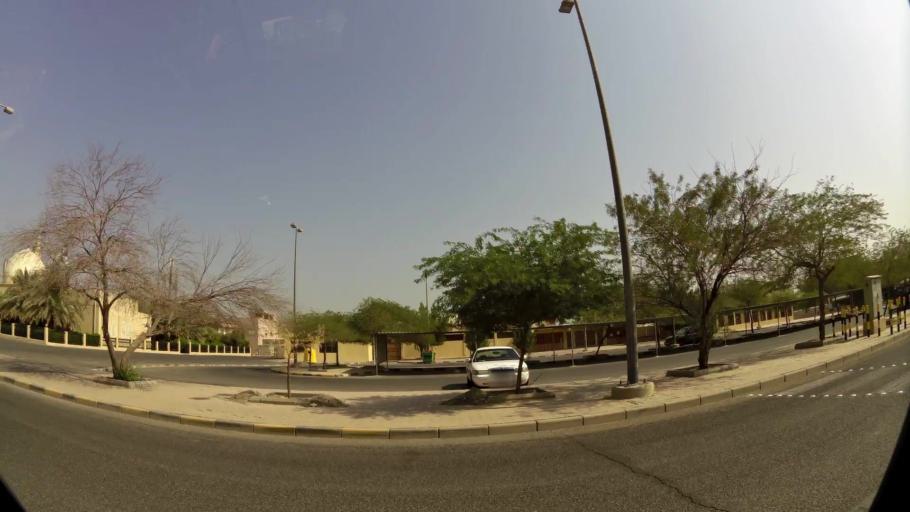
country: KW
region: Al Asimah
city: Ad Dasmah
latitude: 29.3598
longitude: 47.9915
